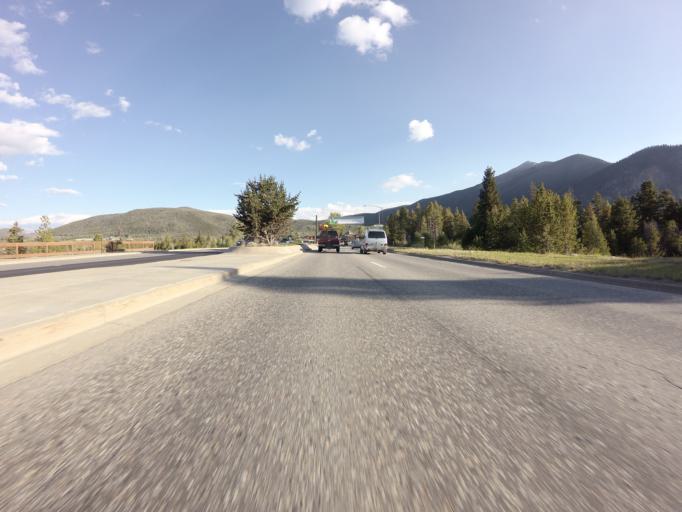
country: US
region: Colorado
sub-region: Summit County
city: Frisco
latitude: 39.5795
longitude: -106.0931
